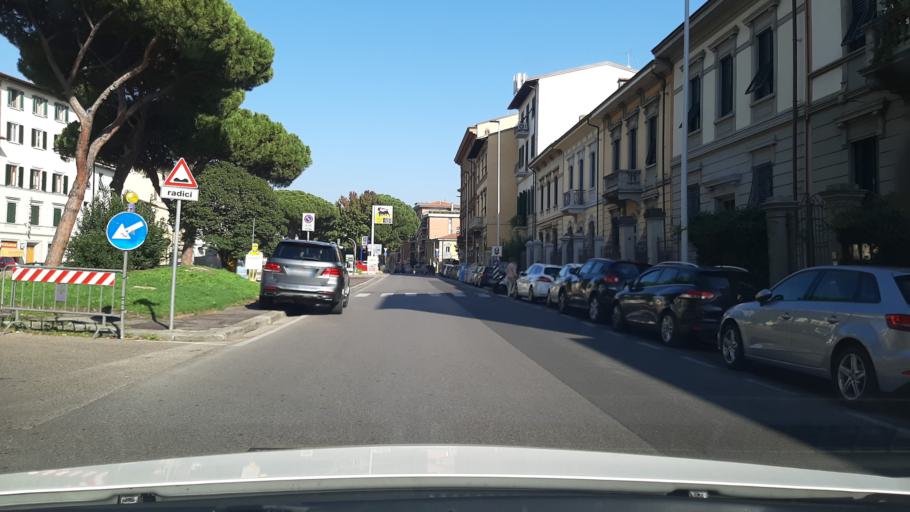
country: IT
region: Tuscany
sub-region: Province of Florence
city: Fiesole
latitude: 43.7737
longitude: 11.2860
